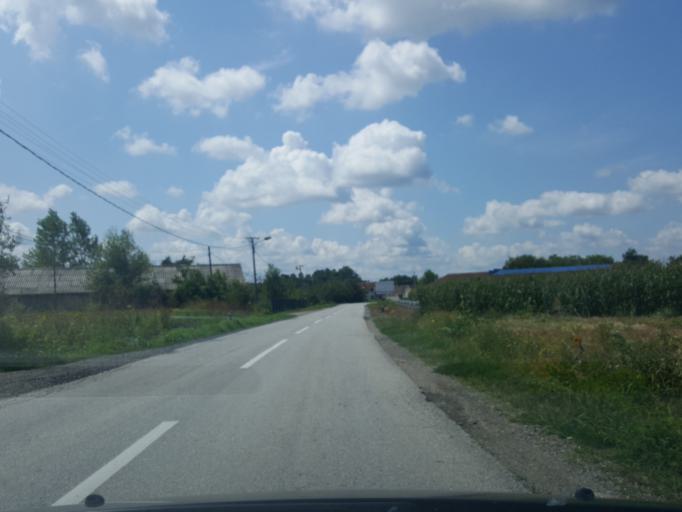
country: RS
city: Metkovic
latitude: 44.8418
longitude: 19.5150
